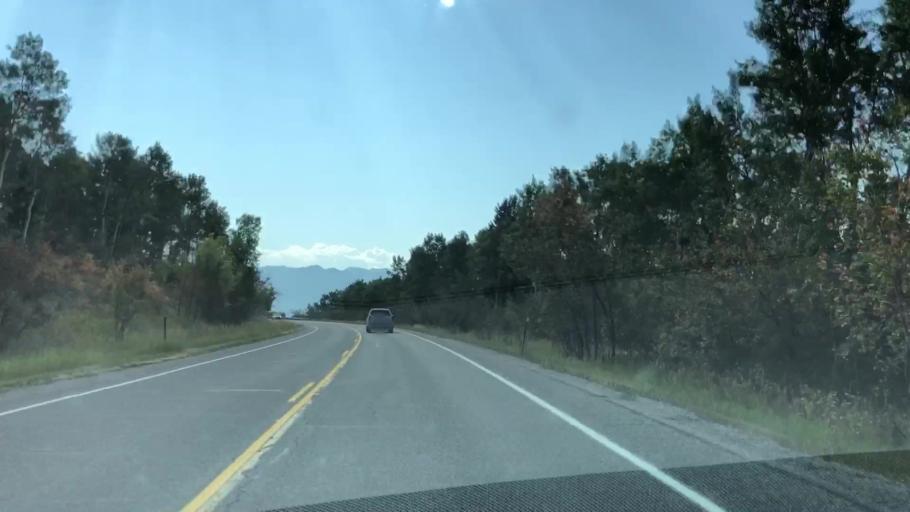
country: US
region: Wyoming
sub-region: Teton County
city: Hoback
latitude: 43.2101
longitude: -111.0584
